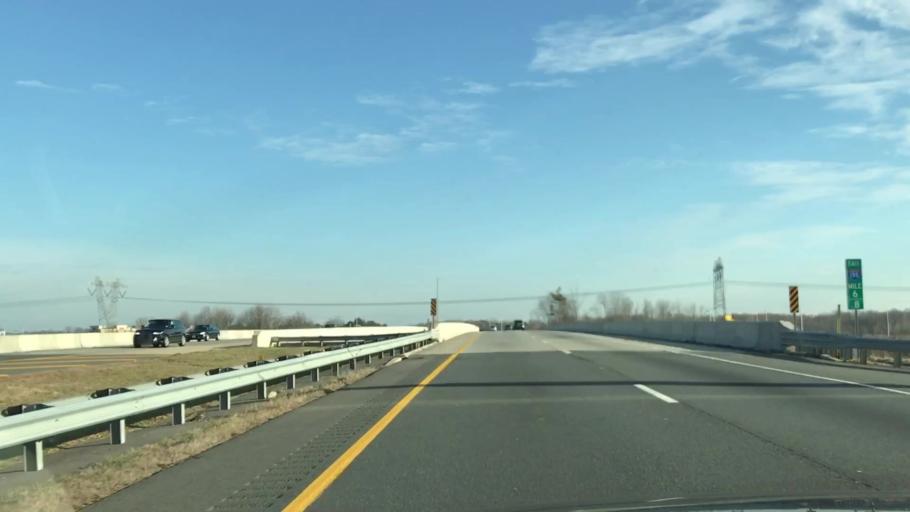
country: US
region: New Jersey
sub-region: Monmouth County
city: Allentown
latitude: 40.1940
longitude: -74.6021
